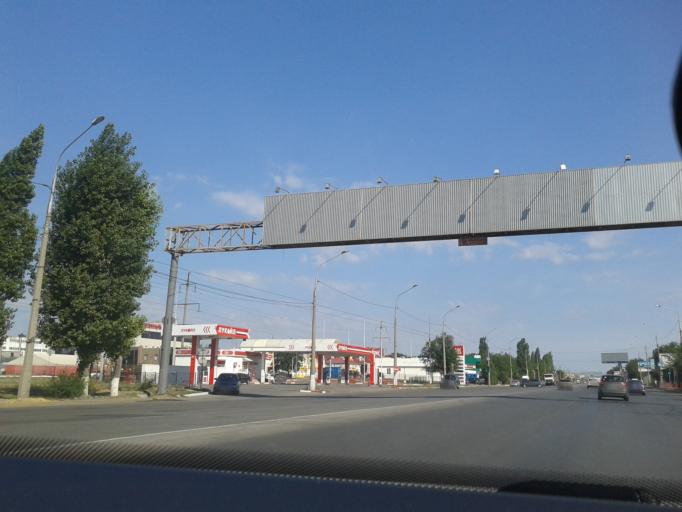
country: RU
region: Volgograd
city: Volgograd
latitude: 48.7568
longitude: 44.4804
